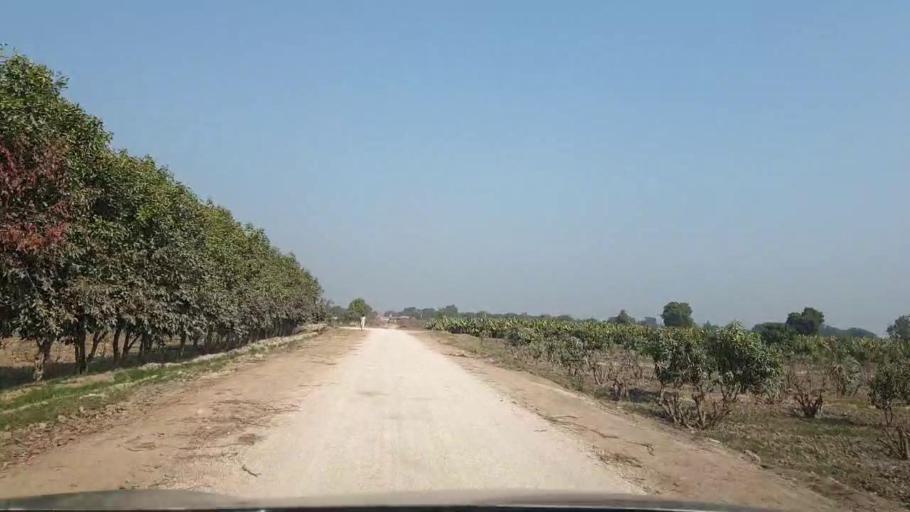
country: PK
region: Sindh
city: Tando Allahyar
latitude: 25.5171
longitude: 68.7631
